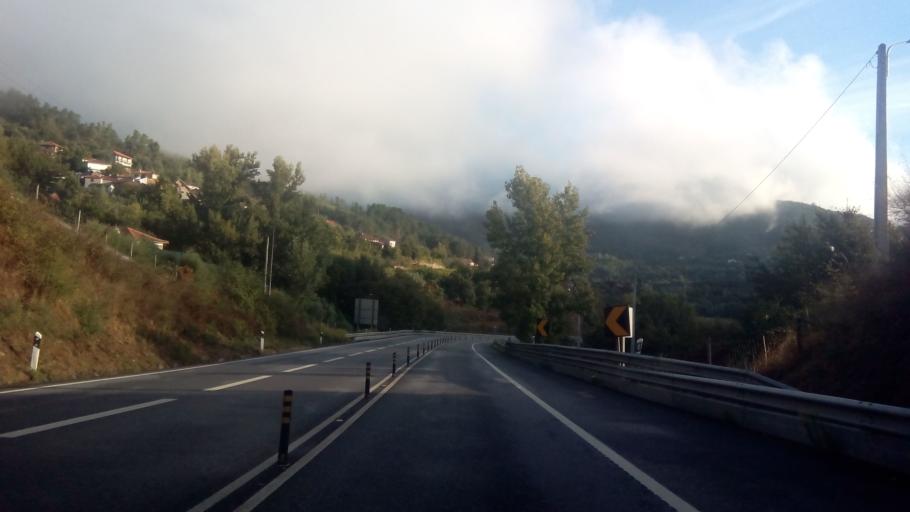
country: PT
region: Porto
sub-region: Amarante
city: Amarante
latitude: 41.2776
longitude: -7.9992
